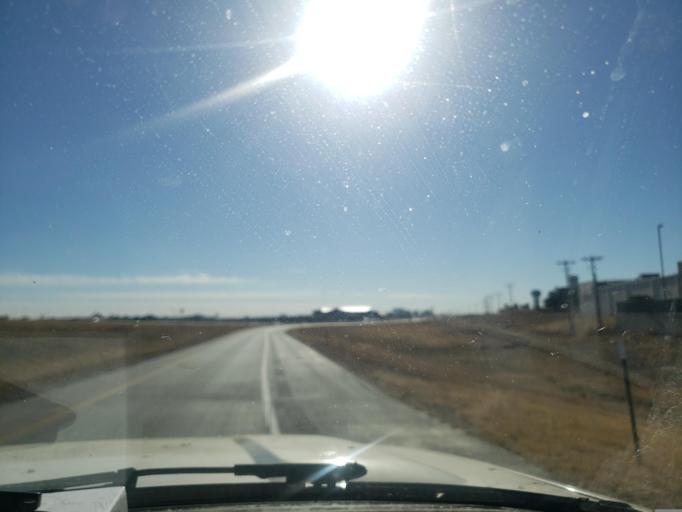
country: US
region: Kansas
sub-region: Finney County
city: Garden City
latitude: 37.9808
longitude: -100.8383
